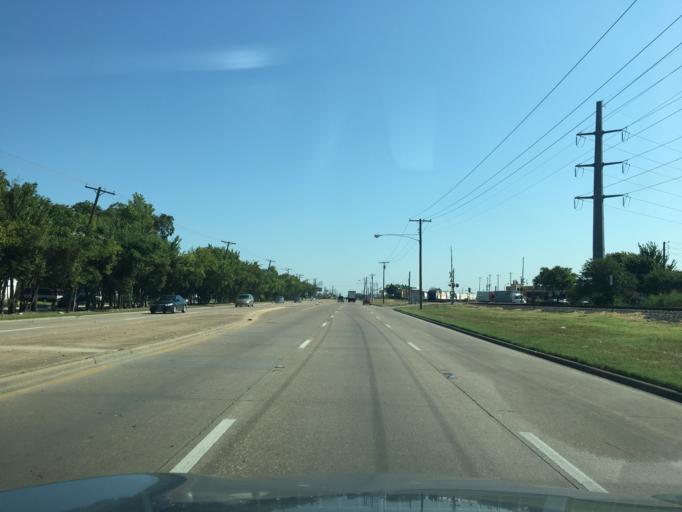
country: US
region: Texas
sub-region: Dallas County
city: Garland
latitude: 32.8549
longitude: -96.6773
